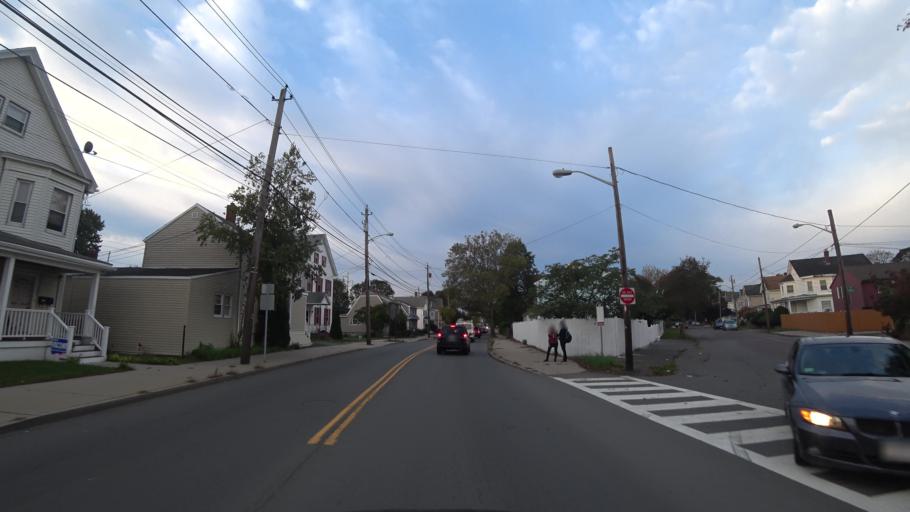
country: US
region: Massachusetts
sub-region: Suffolk County
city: Revere
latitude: 42.4352
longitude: -71.0220
